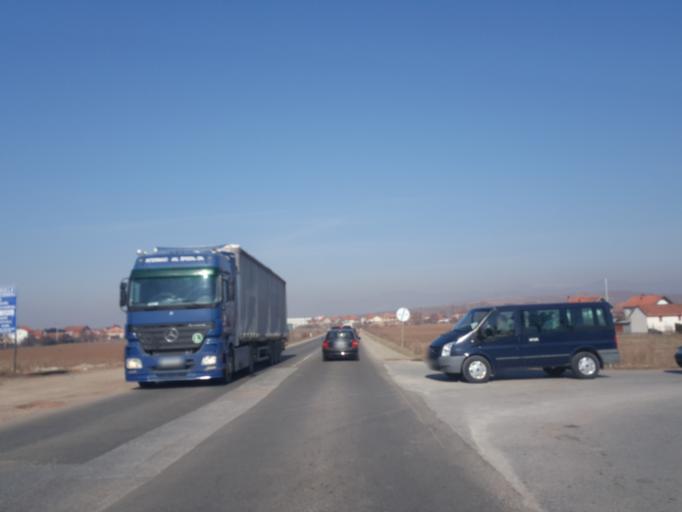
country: XK
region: Mitrovica
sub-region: Vushtrri
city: Vushtrri
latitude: 42.7779
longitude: 21.0144
